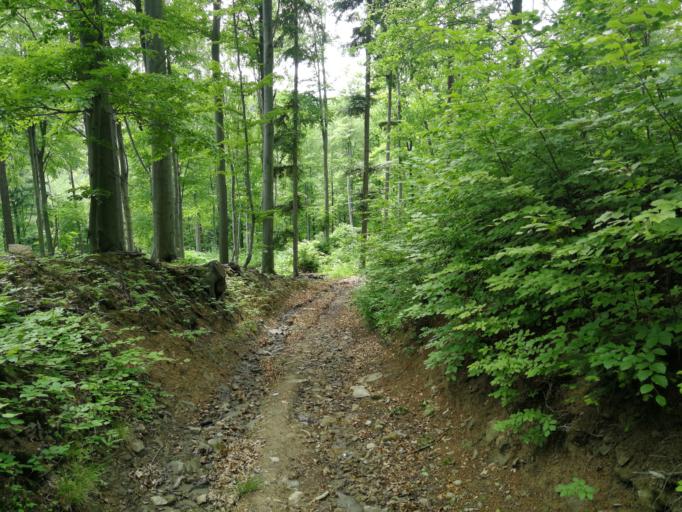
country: PL
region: Lesser Poland Voivodeship
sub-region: Powiat myslenicki
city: Osieczany
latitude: 49.8064
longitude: 19.9670
